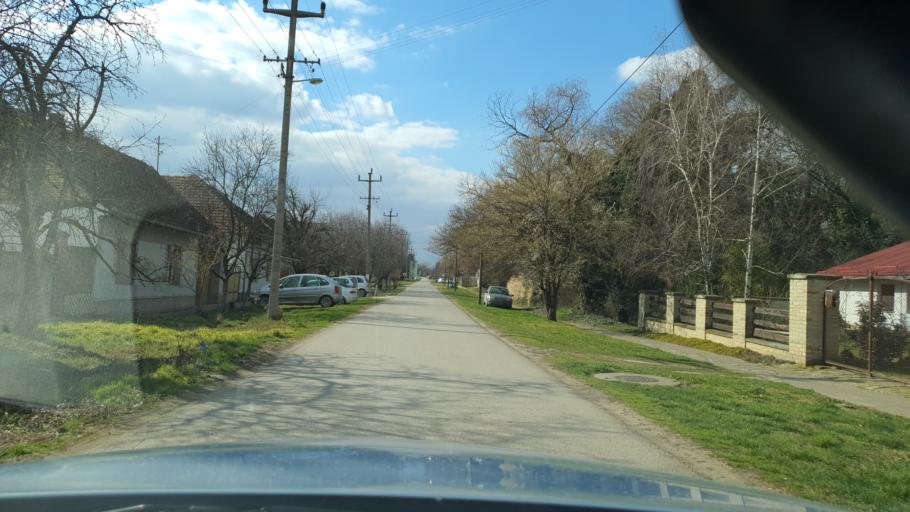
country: RS
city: Kulpin
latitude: 45.4009
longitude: 19.5876
